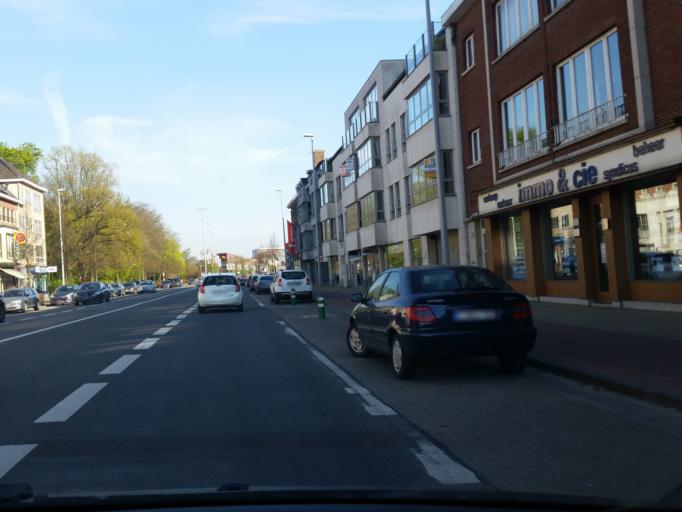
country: BE
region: Flanders
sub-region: Provincie Oost-Vlaanderen
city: Sint-Niklaas
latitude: 51.1627
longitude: 4.1426
